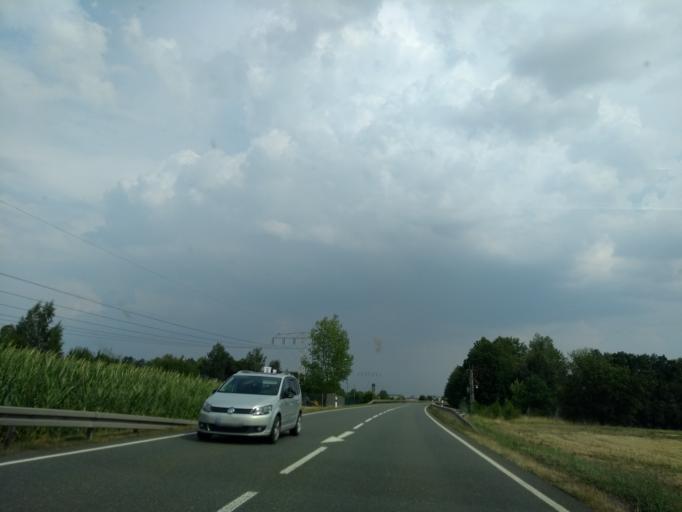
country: DE
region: Thuringia
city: Schwaara
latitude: 50.9366
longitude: 12.1201
